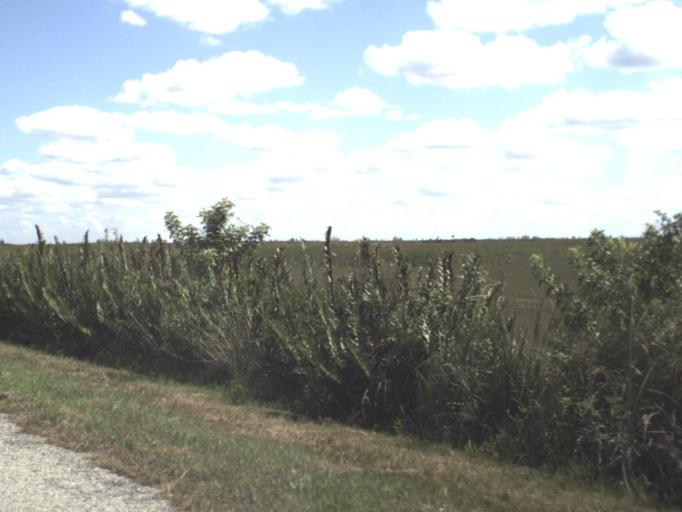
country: US
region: Florida
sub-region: Collier County
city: Marco
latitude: 25.9188
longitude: -81.3958
